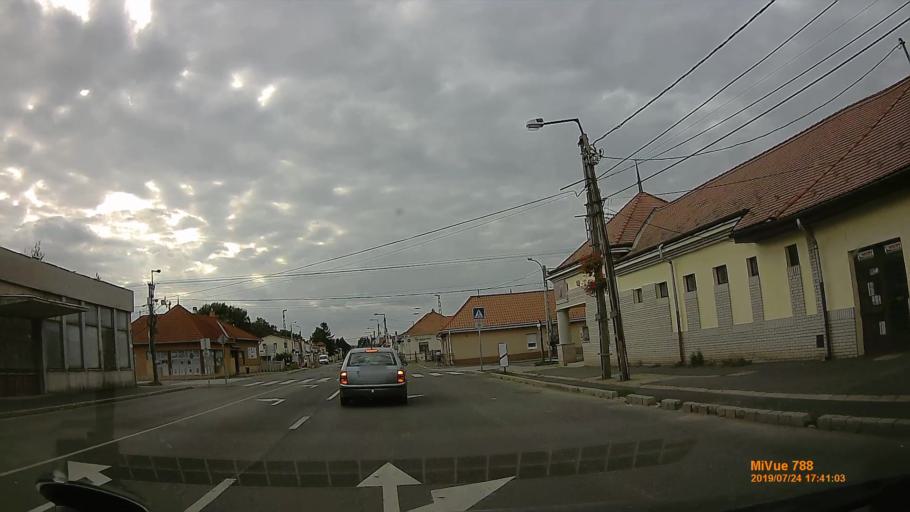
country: HU
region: Borsod-Abauj-Zemplen
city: Encs
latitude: 48.3305
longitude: 21.1224
